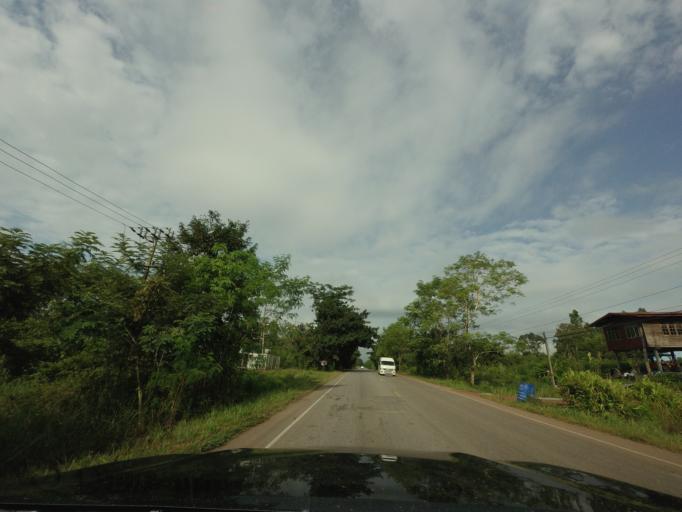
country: TH
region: Changwat Udon Thani
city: Nam Som
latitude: 17.8040
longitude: 102.3030
